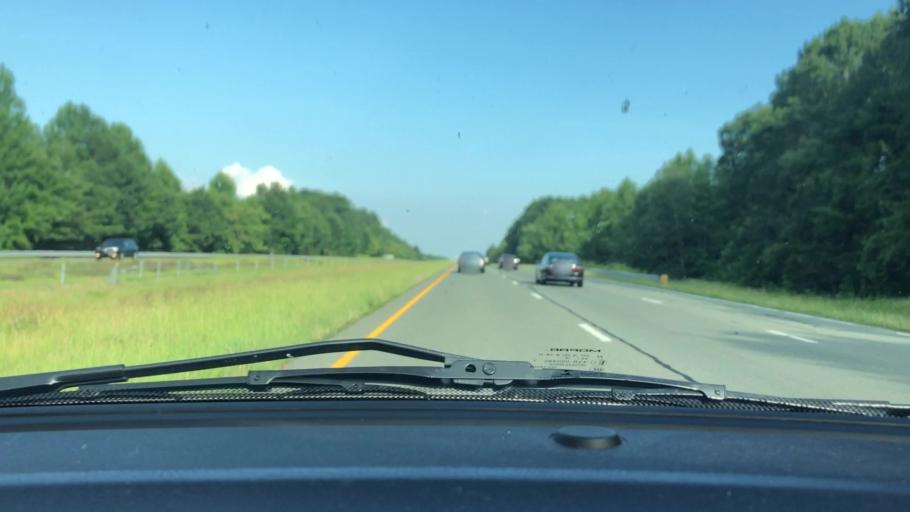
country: US
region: North Carolina
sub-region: Chatham County
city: Siler City
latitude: 35.7608
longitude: -79.4685
